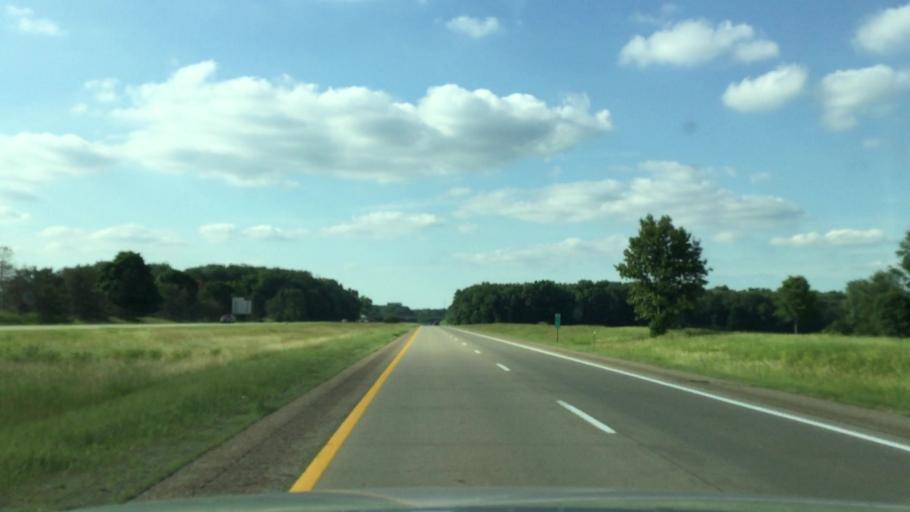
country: US
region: Michigan
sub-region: Branch County
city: Union City
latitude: 42.1236
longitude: -84.9953
